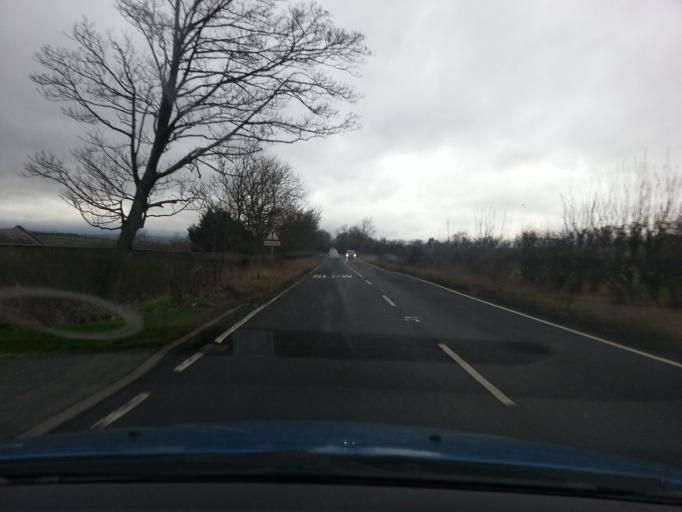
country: GB
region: England
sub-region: County Durham
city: Crook
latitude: 54.6751
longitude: -1.7114
